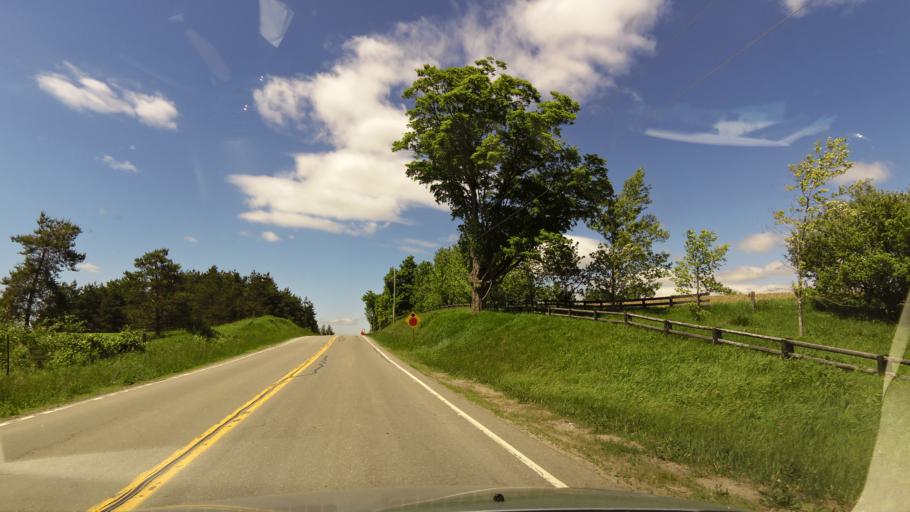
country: CA
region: Ontario
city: Newmarket
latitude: 43.9983
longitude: -79.5468
